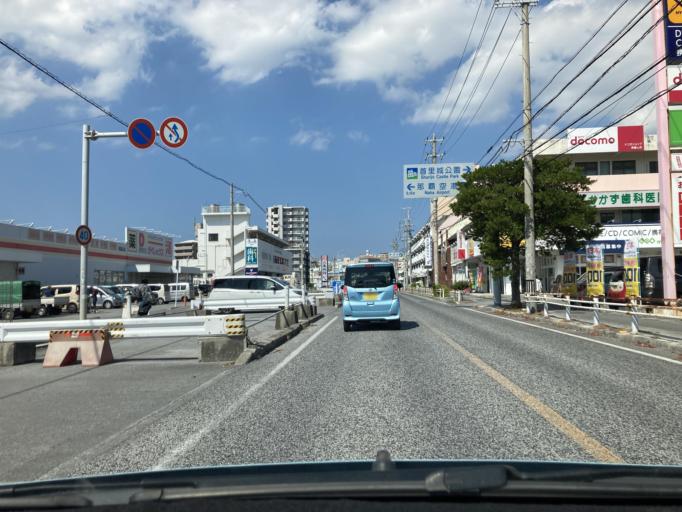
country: JP
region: Okinawa
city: Tomigusuku
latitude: 26.1909
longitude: 127.7081
